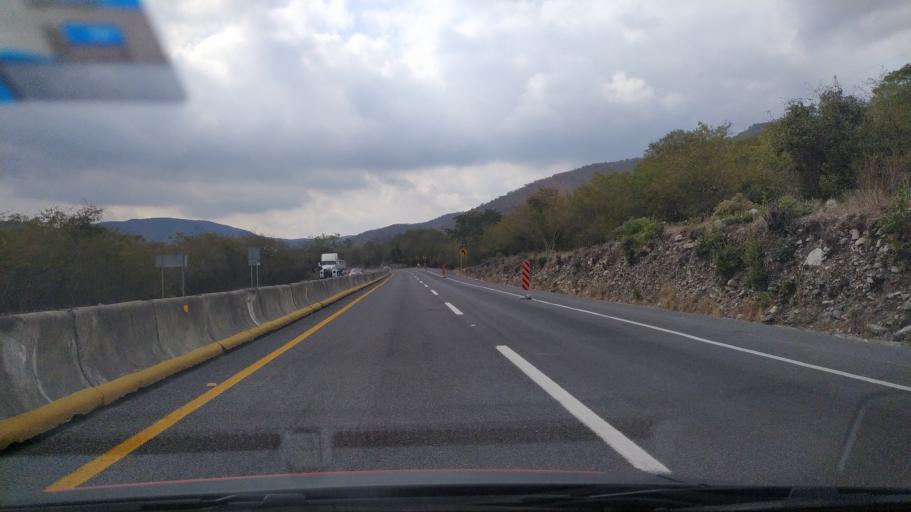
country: MX
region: Colima
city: Ixtlahuacan
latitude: 19.0227
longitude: -103.8108
